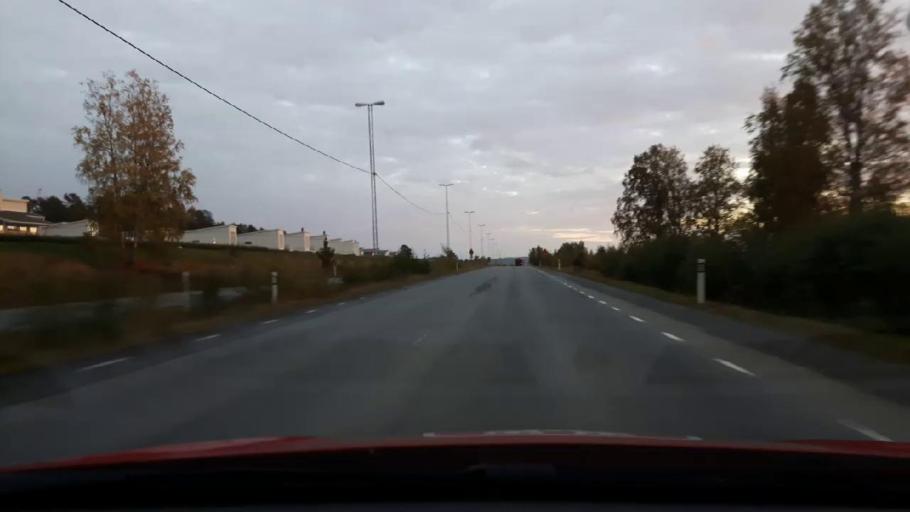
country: SE
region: Jaemtland
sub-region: OEstersunds Kommun
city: Ostersund
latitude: 63.1944
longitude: 14.6442
